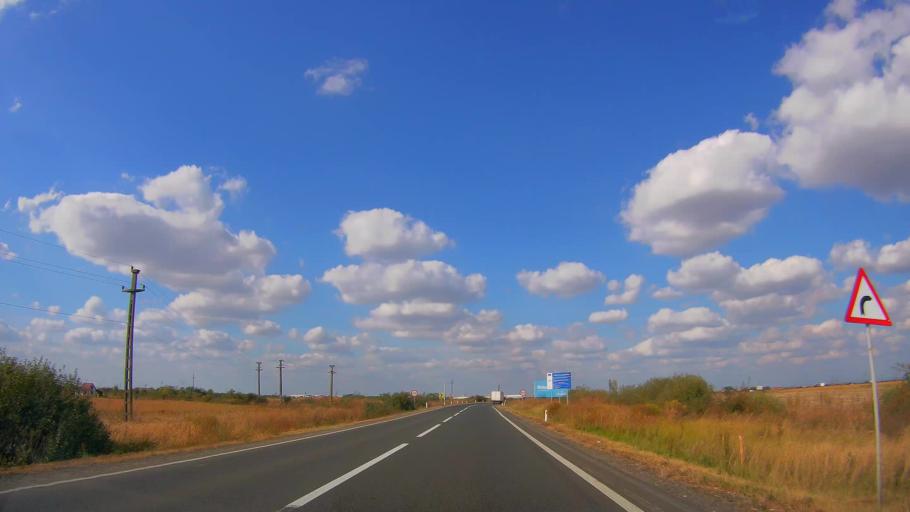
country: RO
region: Satu Mare
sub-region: Oras Ardud
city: Madaras
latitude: 47.7138
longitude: 22.8715
